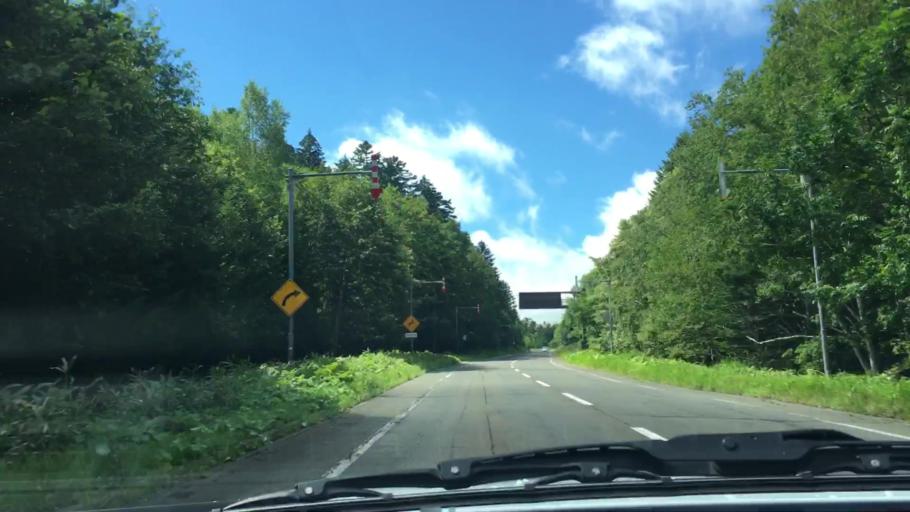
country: JP
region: Hokkaido
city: Kitami
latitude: 43.4456
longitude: 144.0185
